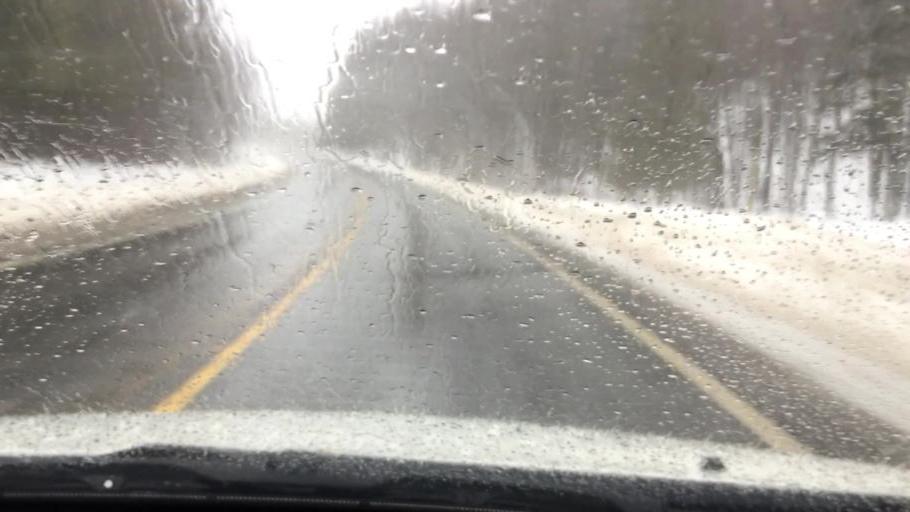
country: US
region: Michigan
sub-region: Antrim County
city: Mancelona
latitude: 45.0007
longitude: -85.0631
